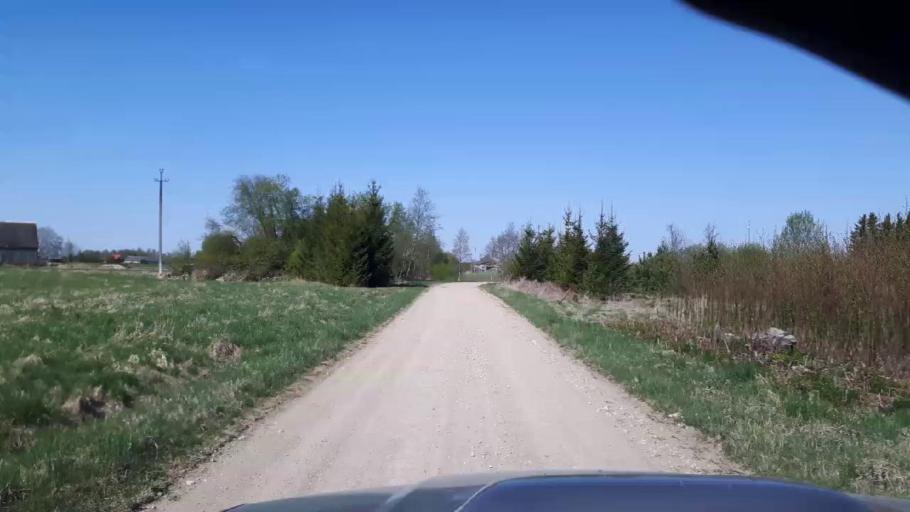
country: EE
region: Paernumaa
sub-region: Sindi linn
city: Sindi
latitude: 58.4448
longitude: 24.7834
